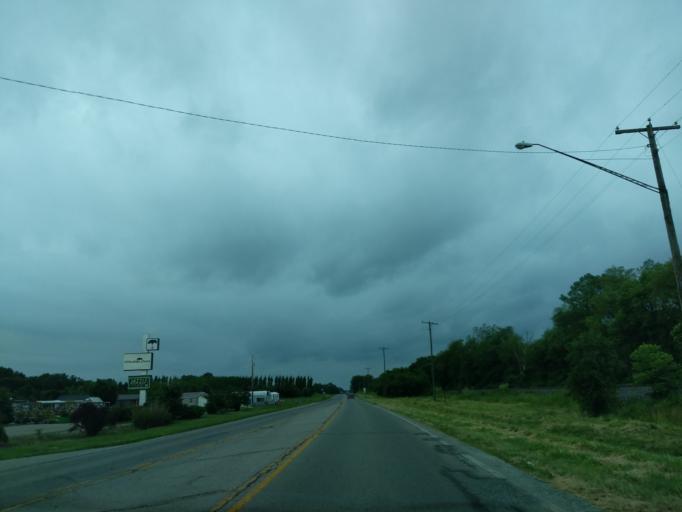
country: US
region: Indiana
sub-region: Madison County
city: Chesterfield
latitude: 40.1070
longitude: -85.5970
